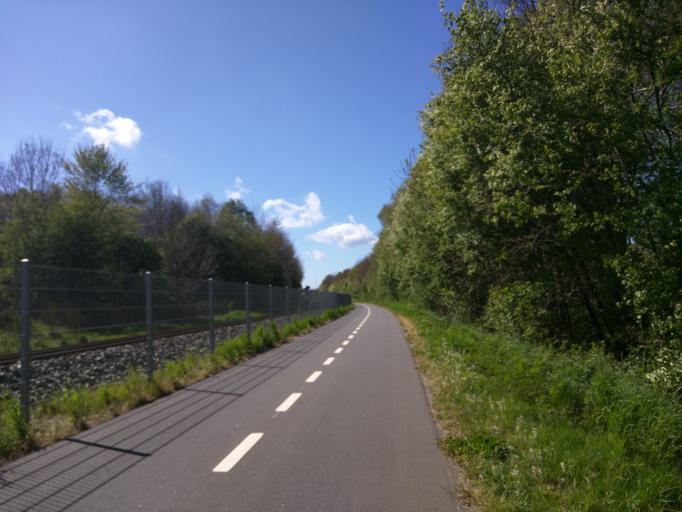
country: DK
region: Central Jutland
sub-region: Viborg Kommune
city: Viborg
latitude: 56.4550
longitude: 9.3762
